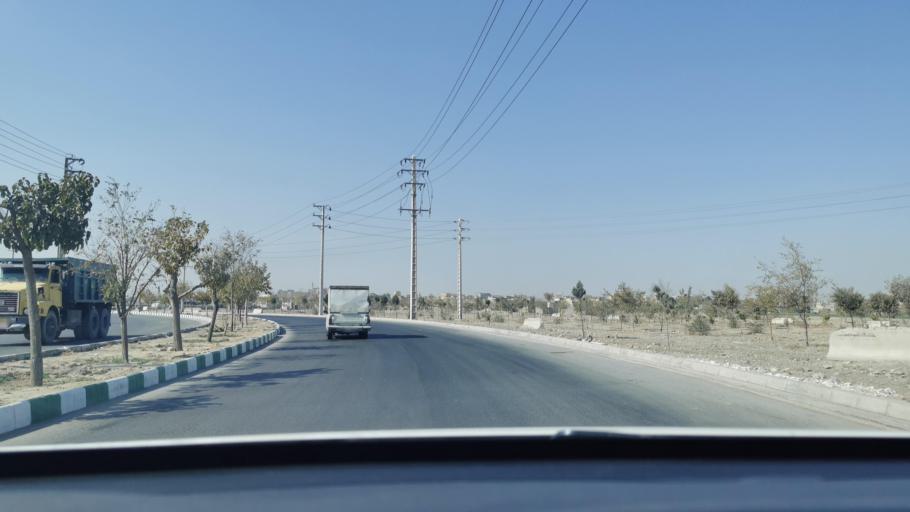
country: IR
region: Razavi Khorasan
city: Mashhad
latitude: 36.3476
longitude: 59.6110
